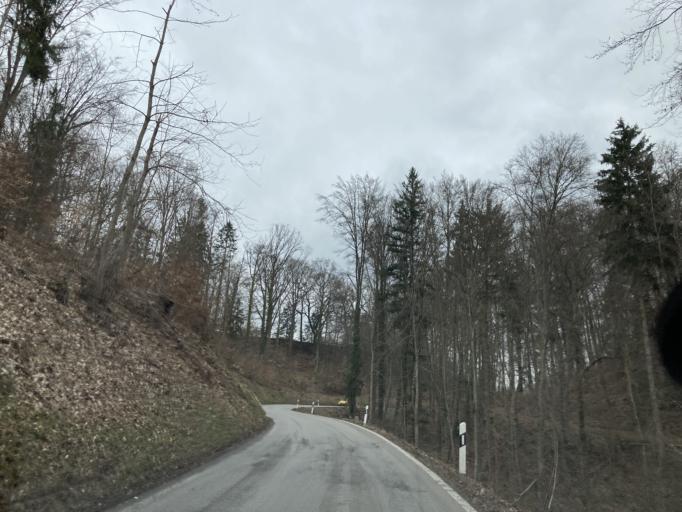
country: DE
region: Baden-Wuerttemberg
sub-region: Regierungsbezirk Stuttgart
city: Bondorf
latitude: 48.4531
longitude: 8.8141
